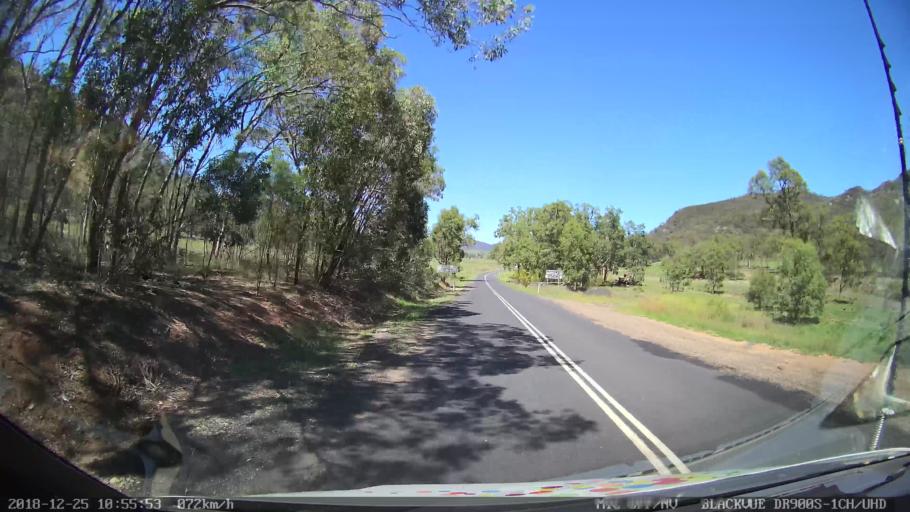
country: AU
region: New South Wales
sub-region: Upper Hunter Shire
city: Merriwa
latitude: -32.3985
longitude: 150.2687
